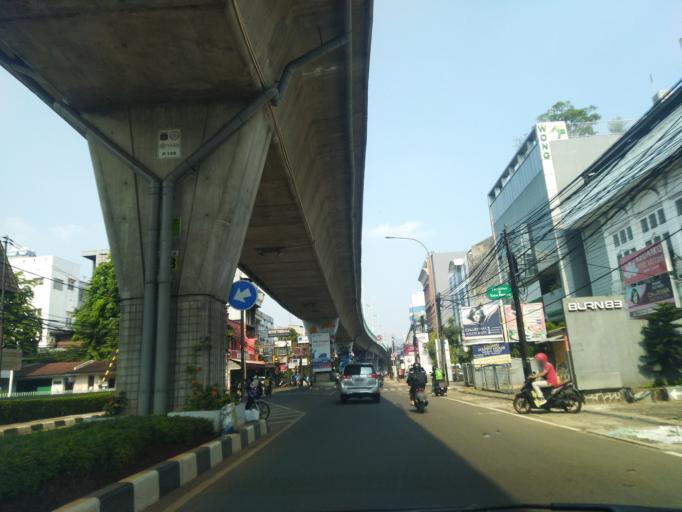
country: ID
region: Jakarta Raya
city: Jakarta
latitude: -6.2388
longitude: 106.8131
